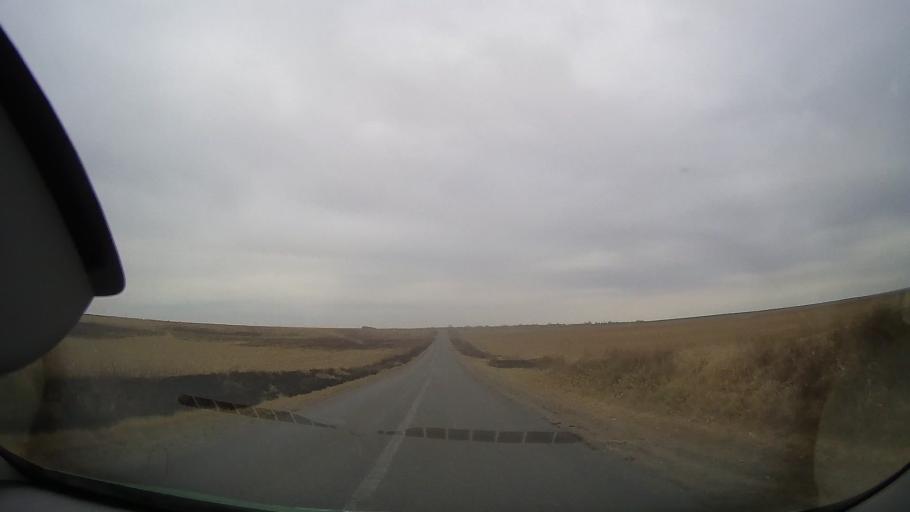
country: RO
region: Buzau
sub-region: Comuna Rusetu
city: Rusetu
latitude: 44.9669
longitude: 27.1955
